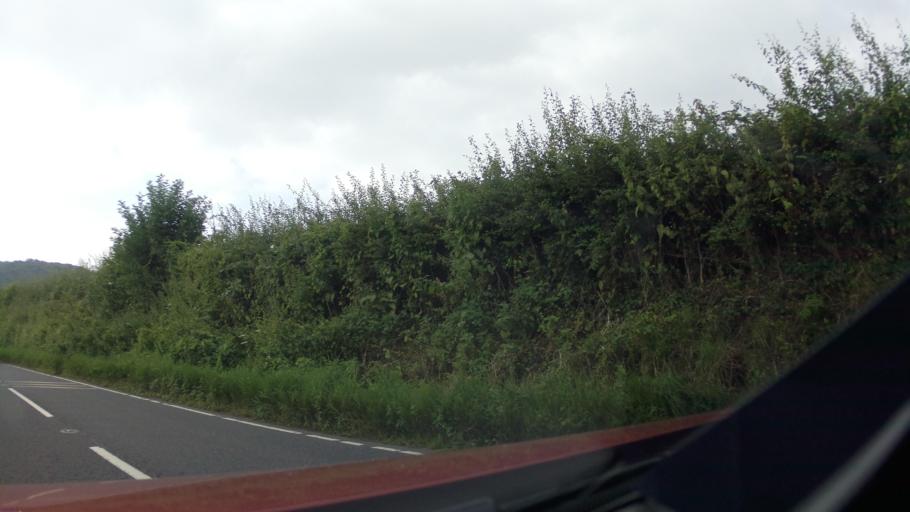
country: GB
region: England
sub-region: North Somerset
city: Easton-in-Gordano
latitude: 51.4715
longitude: -2.7205
